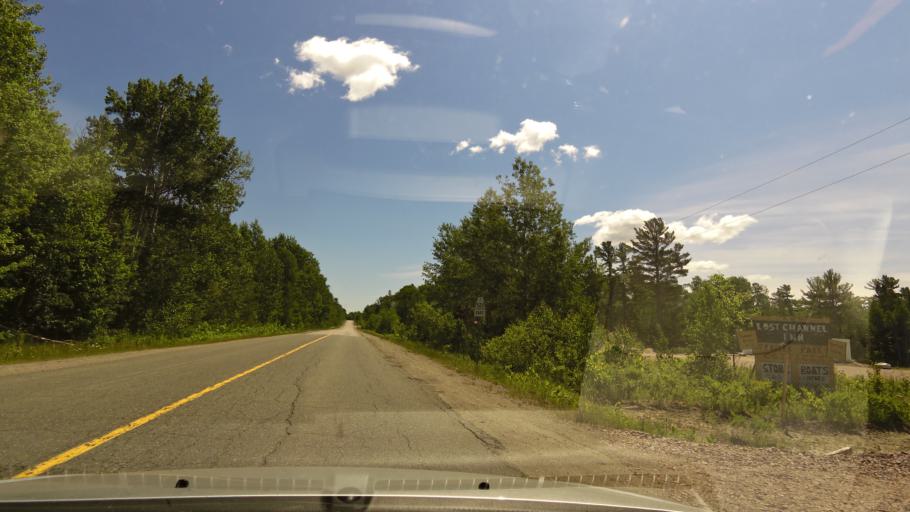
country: CA
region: Ontario
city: Greater Sudbury
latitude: 45.9128
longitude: -80.5597
